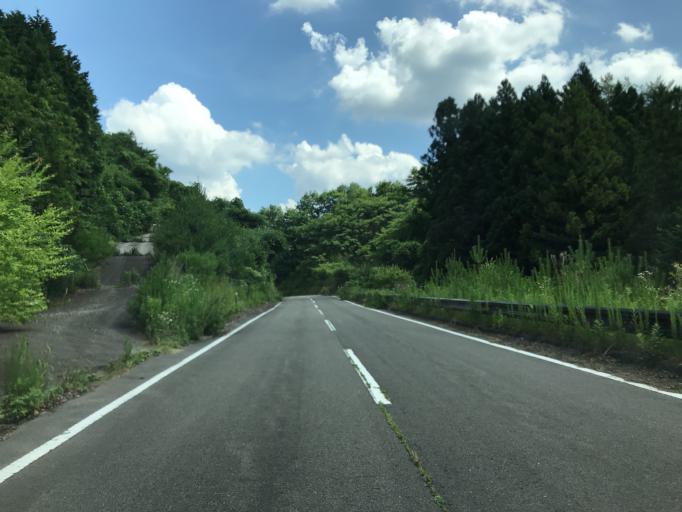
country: JP
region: Fukushima
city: Yanagawamachi-saiwaicho
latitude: 37.7724
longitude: 140.6718
